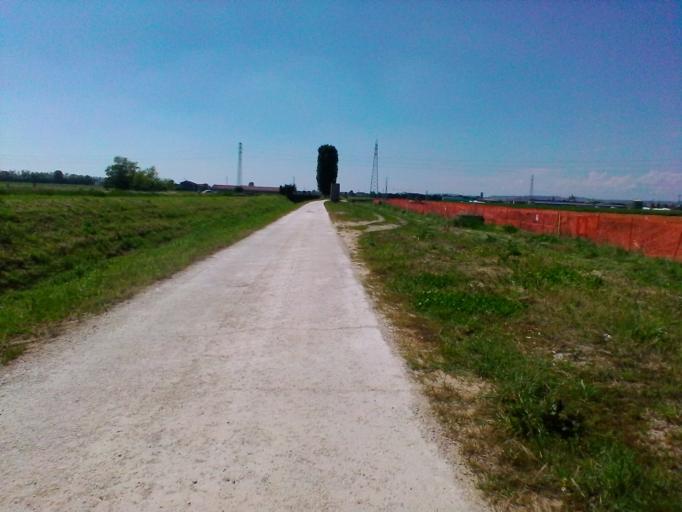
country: IT
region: Veneto
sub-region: Provincia di Verona
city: Povegliano Veronese
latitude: 45.3402
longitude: 10.8667
